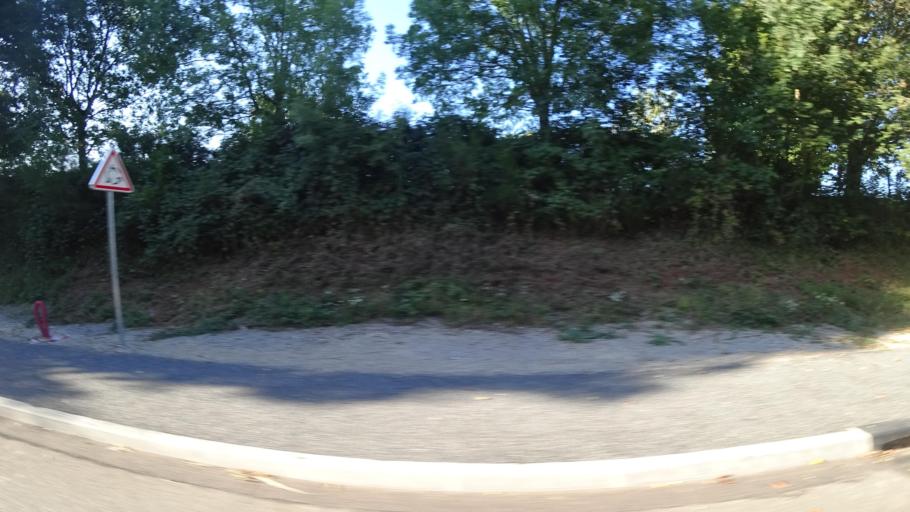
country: FR
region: Midi-Pyrenees
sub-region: Departement de l'Aveyron
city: Olemps
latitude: 44.3257
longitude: 2.5561
